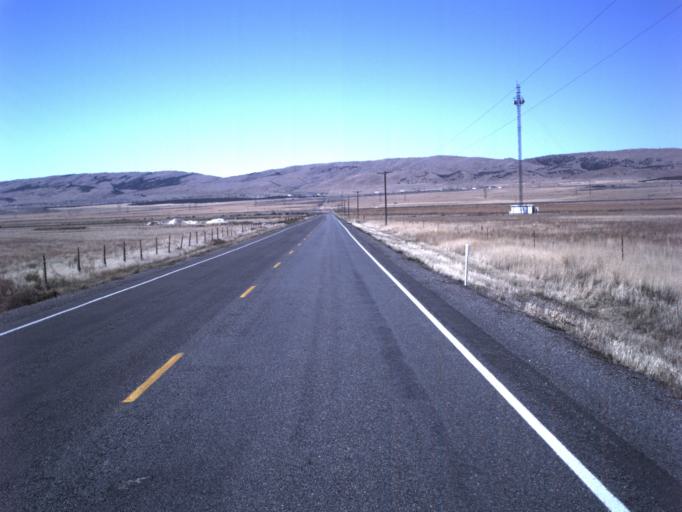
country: US
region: Utah
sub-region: Juab County
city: Nephi
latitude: 39.5580
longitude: -111.8973
